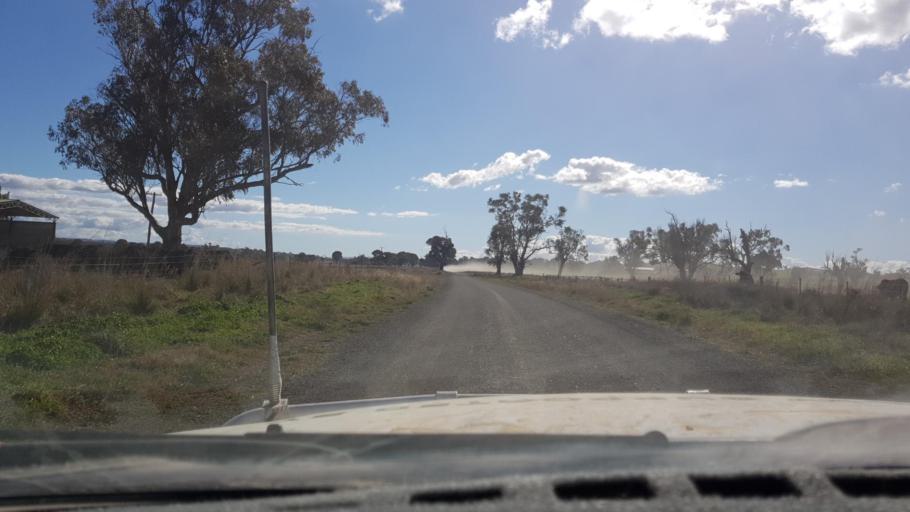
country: AU
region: New South Wales
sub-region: Narrabri
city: Blair Athol
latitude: -30.5303
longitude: 150.4427
